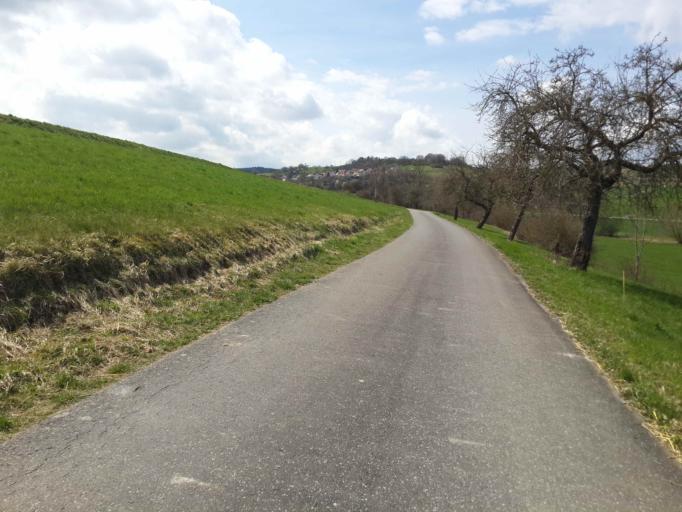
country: DE
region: Baden-Wuerttemberg
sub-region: Regierungsbezirk Stuttgart
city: Bad Mergentheim
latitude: 49.4509
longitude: 9.7612
